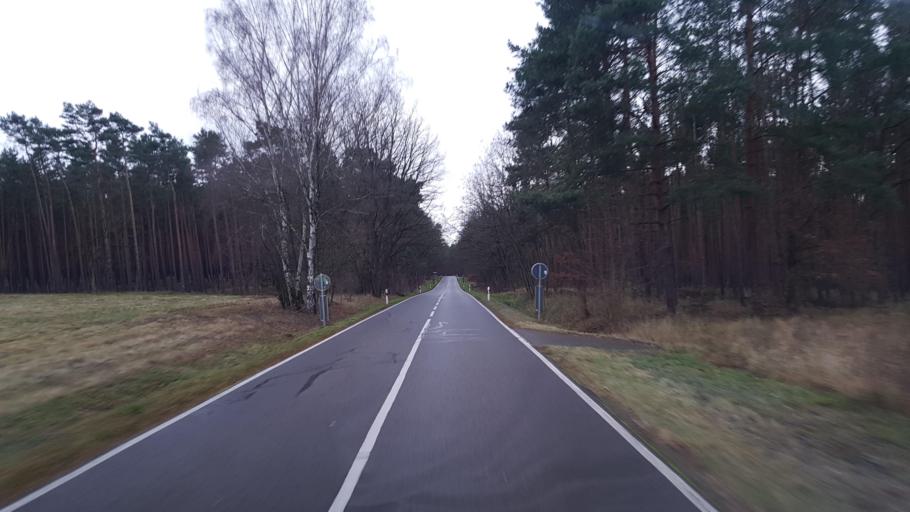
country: DE
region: Brandenburg
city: Schlepzig
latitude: 52.0169
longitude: 13.9772
